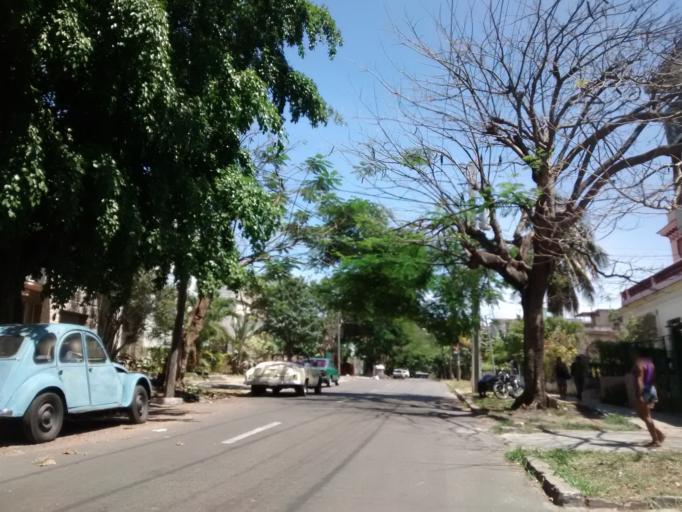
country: CU
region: La Habana
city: Havana
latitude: 23.1289
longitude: -82.4042
